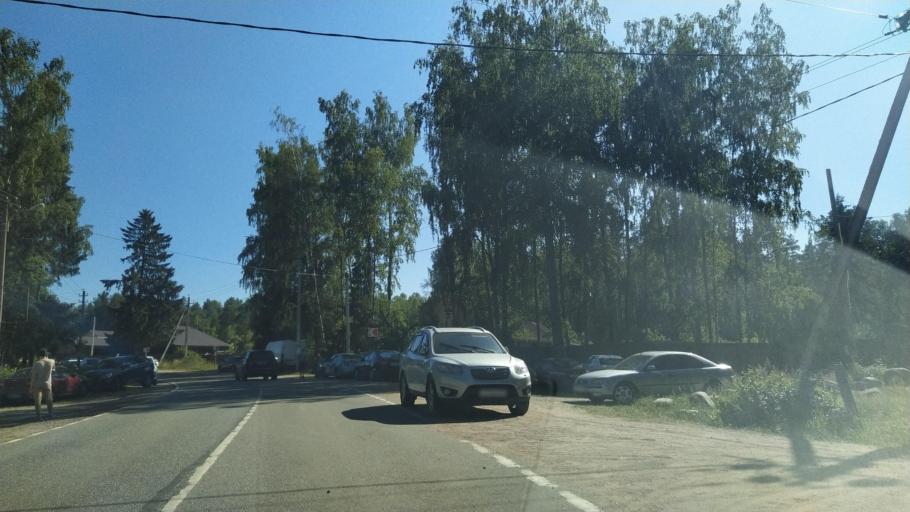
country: RU
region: Leningrad
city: Borisova Griva
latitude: 60.1211
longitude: 31.0740
